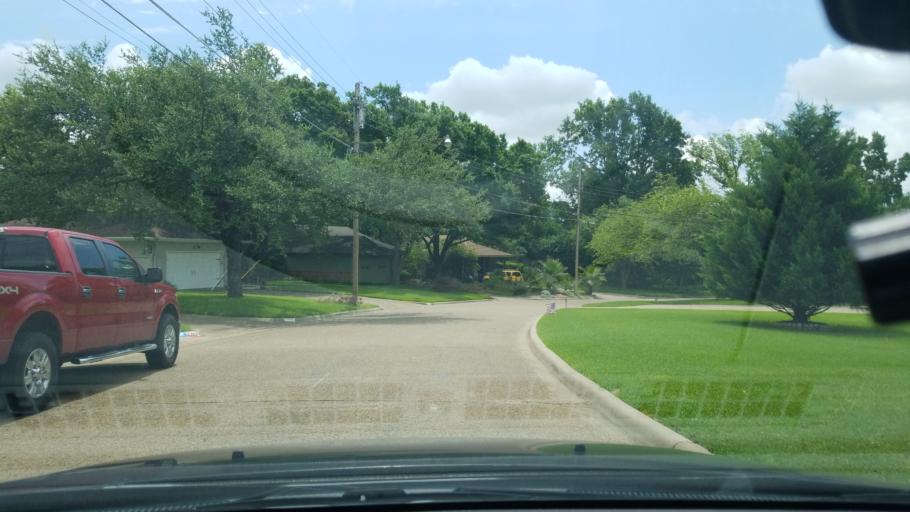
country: US
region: Texas
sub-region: Dallas County
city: Garland
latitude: 32.8286
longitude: -96.6868
